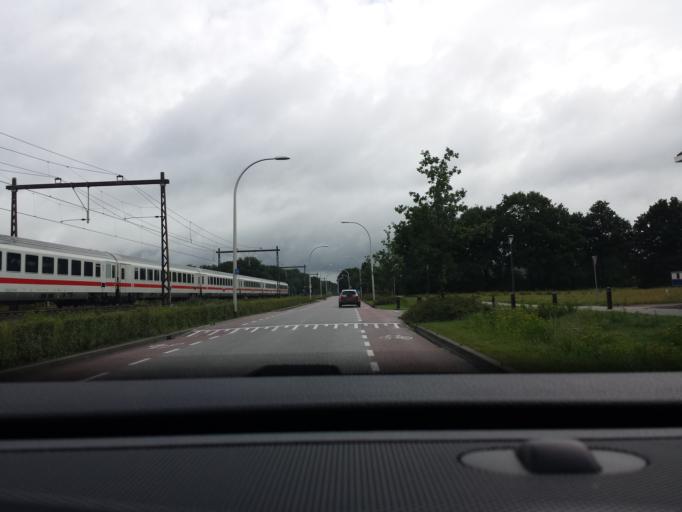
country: NL
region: Overijssel
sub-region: Gemeente Hof van Twente
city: Markelo
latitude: 52.2855
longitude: 6.4302
